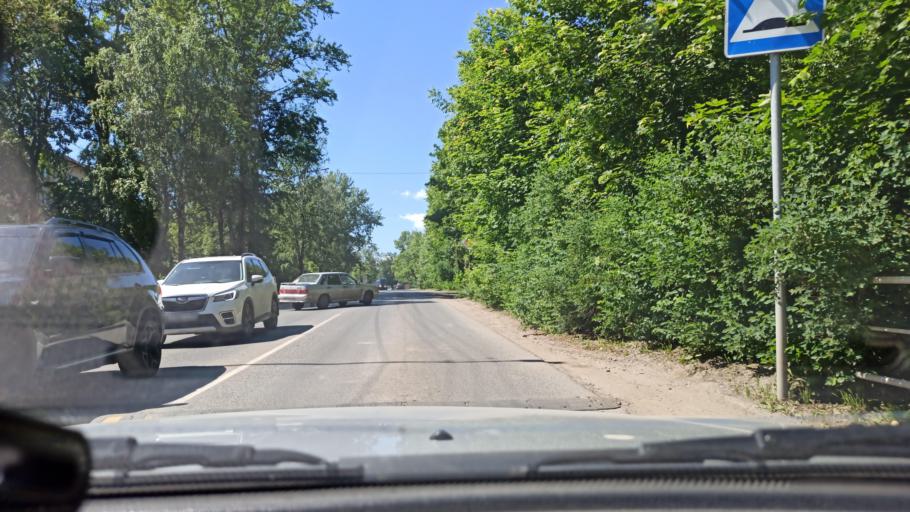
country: RU
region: Vologda
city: Vologda
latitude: 59.2130
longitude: 39.8408
